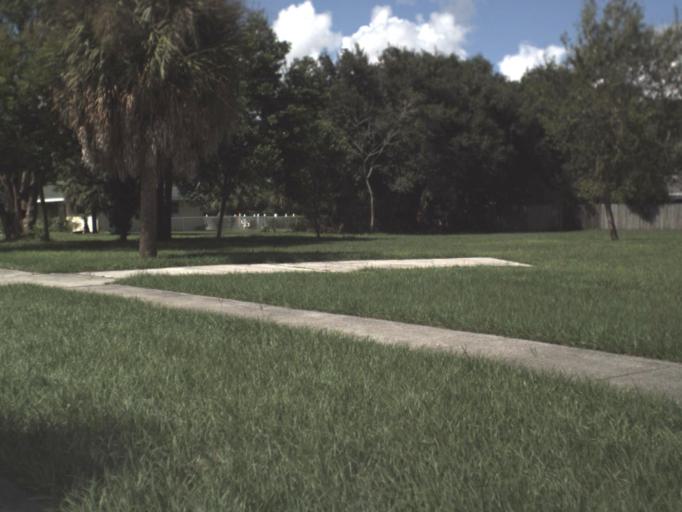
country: US
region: Florida
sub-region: DeSoto County
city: Arcadia
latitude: 27.2191
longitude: -81.8671
